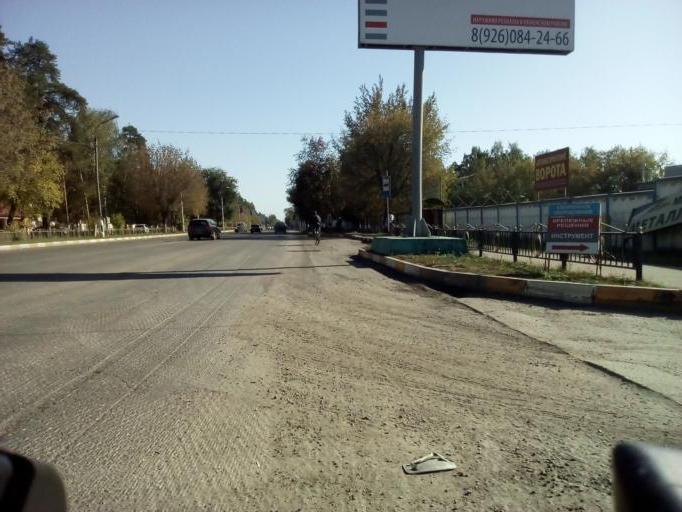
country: RU
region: Moskovskaya
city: Ramenskoye
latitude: 55.5611
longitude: 38.2483
